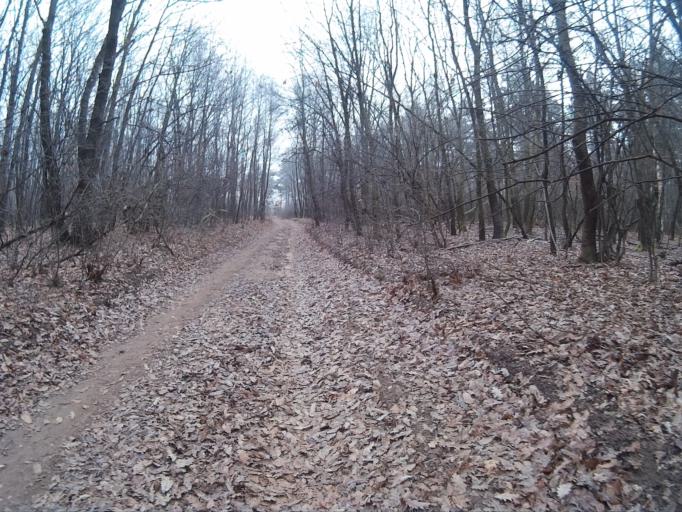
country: HU
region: Komarom-Esztergom
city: Oroszlany
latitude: 47.4369
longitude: 18.3502
